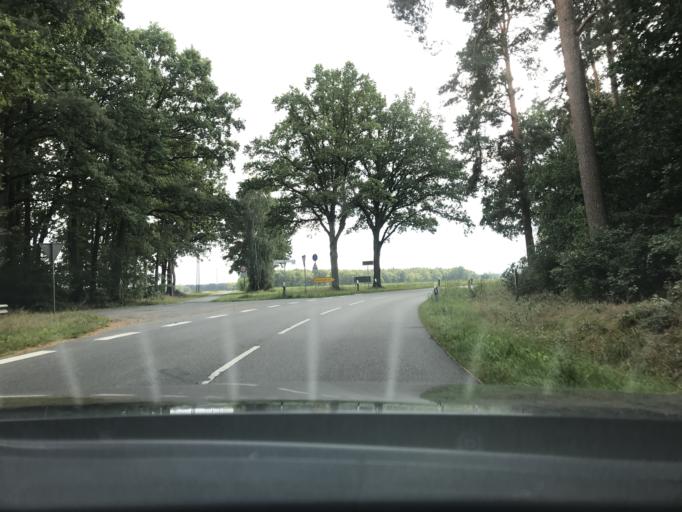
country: DE
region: Lower Saxony
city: Suderburg
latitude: 52.8842
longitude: 10.4429
